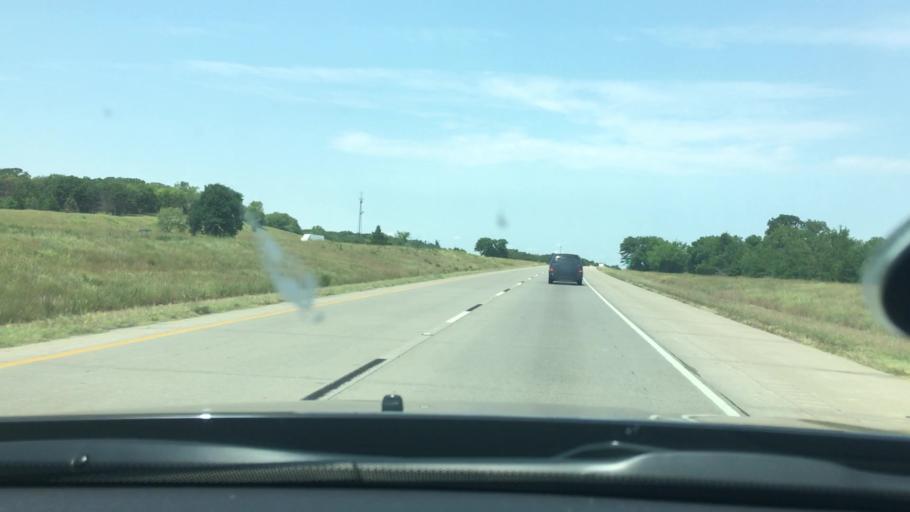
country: US
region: Oklahoma
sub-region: Love County
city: Marietta
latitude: 33.9924
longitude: -97.1392
